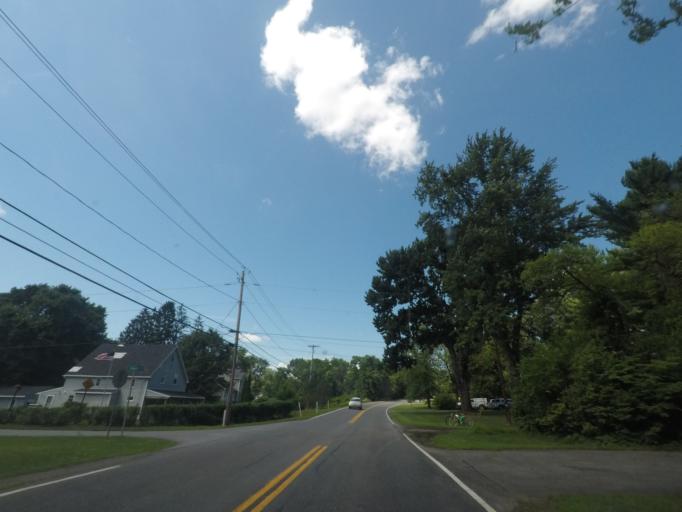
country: US
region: New York
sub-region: Schenectady County
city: Rotterdam
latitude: 42.7647
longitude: -73.9625
